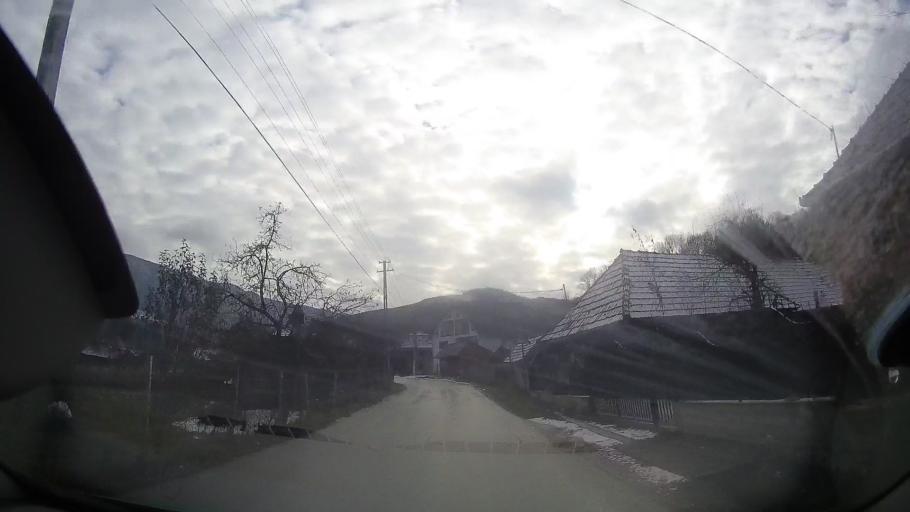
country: RO
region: Alba
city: Salciua de Sus
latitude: 46.4299
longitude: 23.4404
